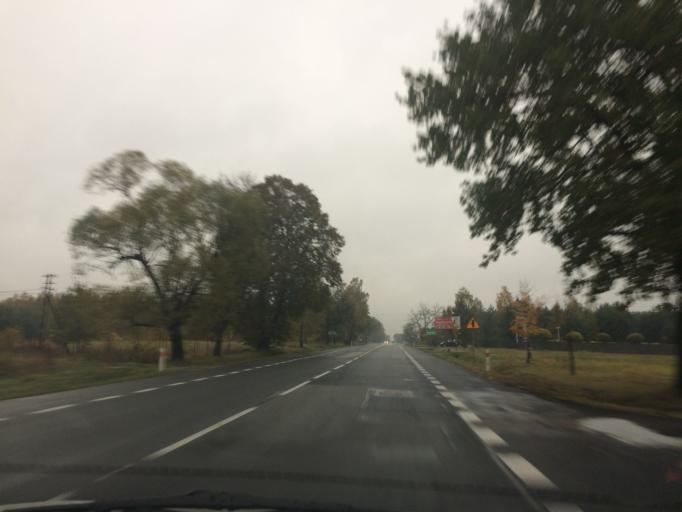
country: PL
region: Masovian Voivodeship
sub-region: Powiat otwocki
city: Celestynow
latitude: 52.0946
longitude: 21.4128
